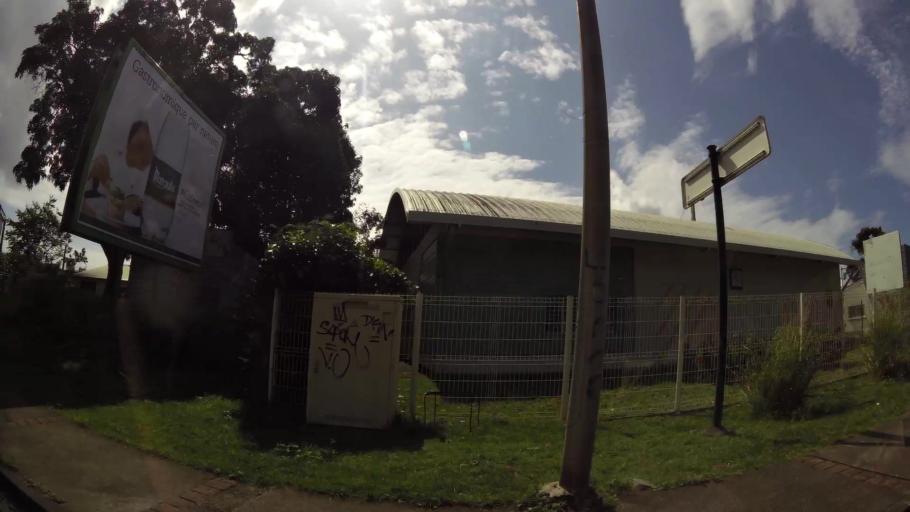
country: GP
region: Guadeloupe
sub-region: Guadeloupe
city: Basse-Terre
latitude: 16.0036
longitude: -61.7283
